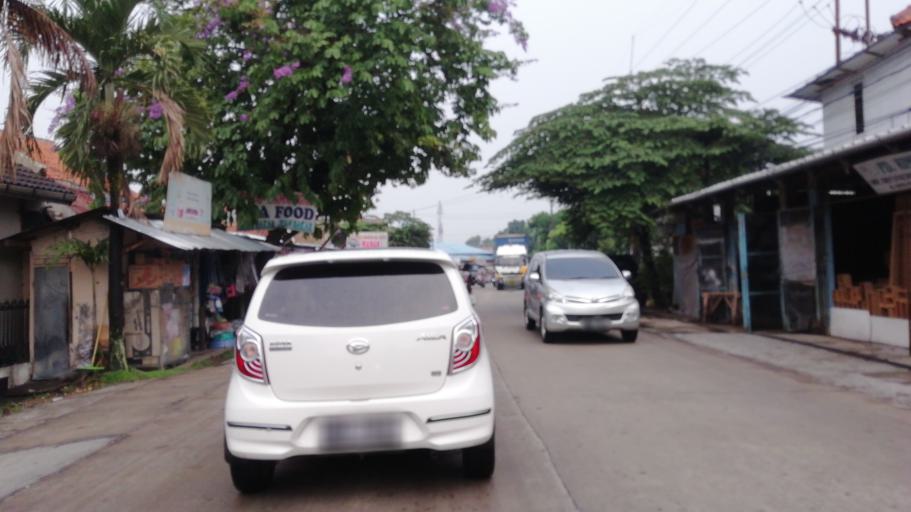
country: ID
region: West Java
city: Bogor
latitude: -6.5556
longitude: 106.8110
